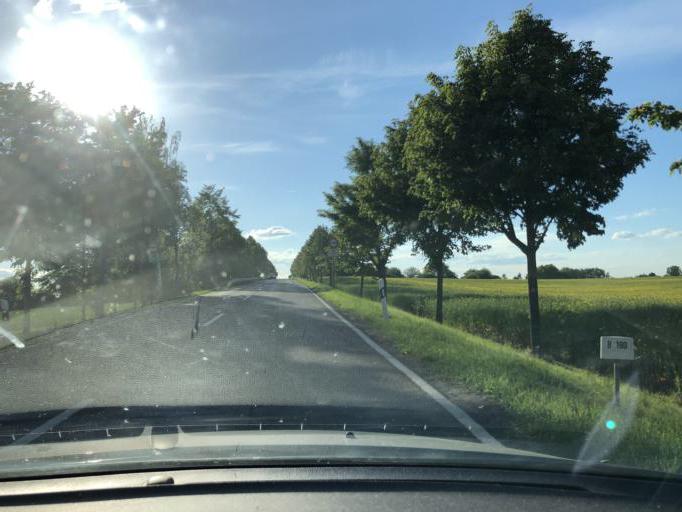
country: DE
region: Thuringia
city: Rositz
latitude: 51.0213
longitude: 12.3650
